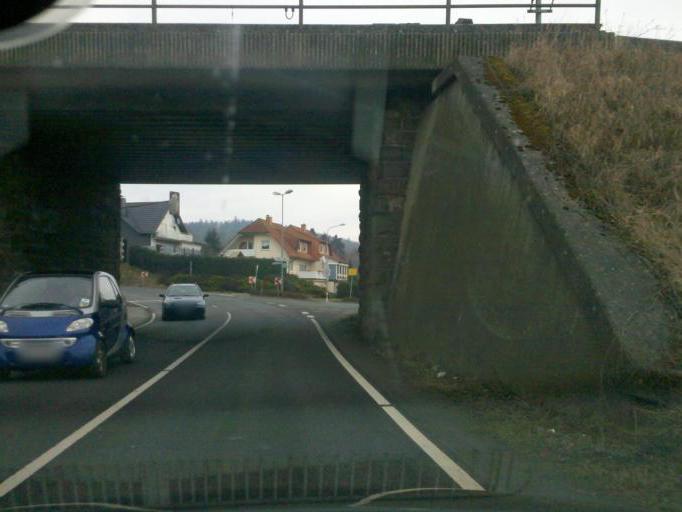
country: DE
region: Hesse
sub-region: Regierungsbezirk Giessen
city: Haiger
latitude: 50.7485
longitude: 8.2068
